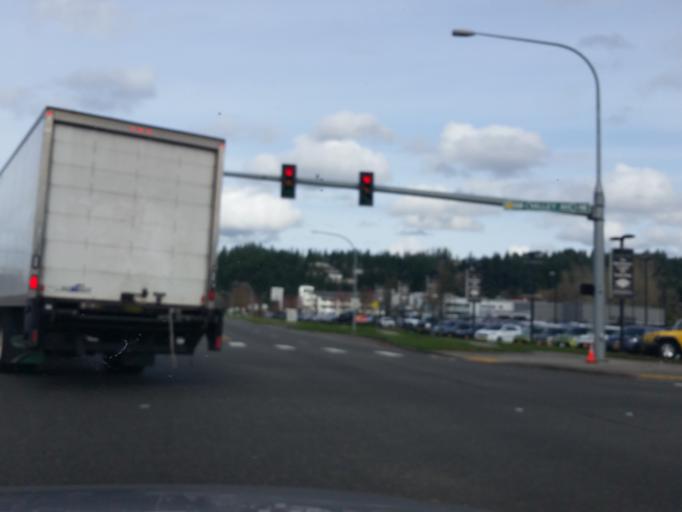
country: US
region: Washington
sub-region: Pierce County
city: North Puyallup
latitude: 47.2061
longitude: -122.2938
